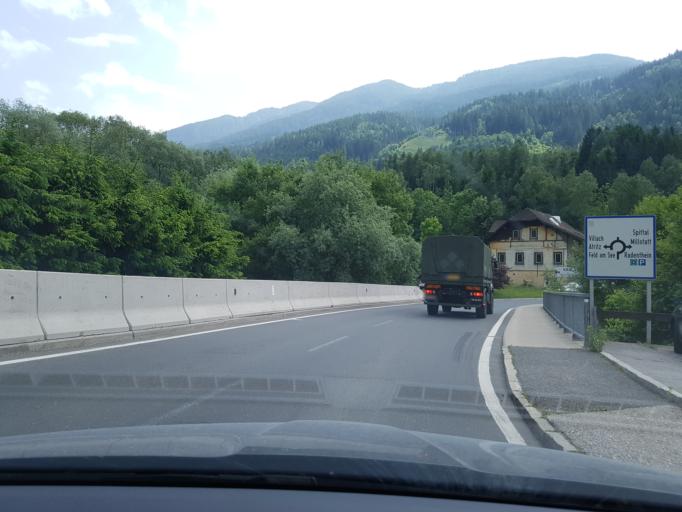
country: AT
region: Carinthia
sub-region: Politischer Bezirk Spittal an der Drau
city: Radenthein
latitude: 46.7988
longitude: 13.7148
